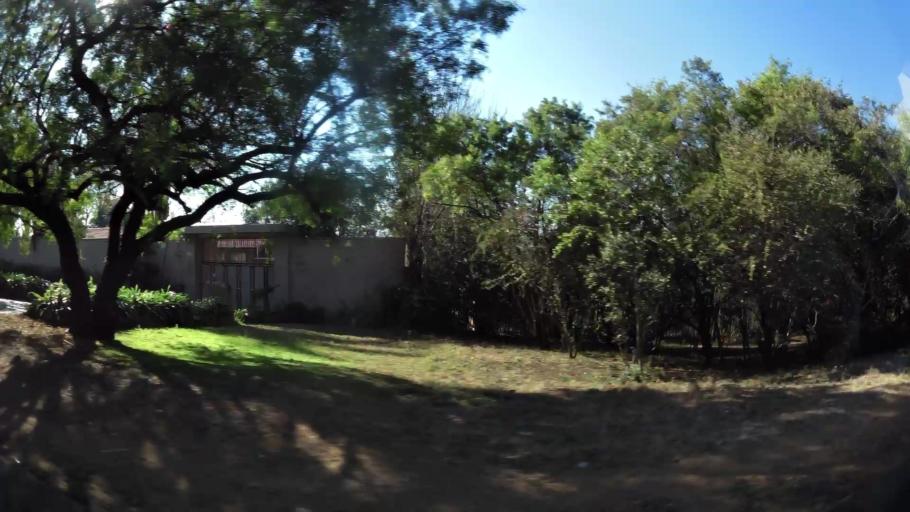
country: ZA
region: Gauteng
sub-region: City of Johannesburg Metropolitan Municipality
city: Midrand
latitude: -26.0496
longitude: 28.0337
